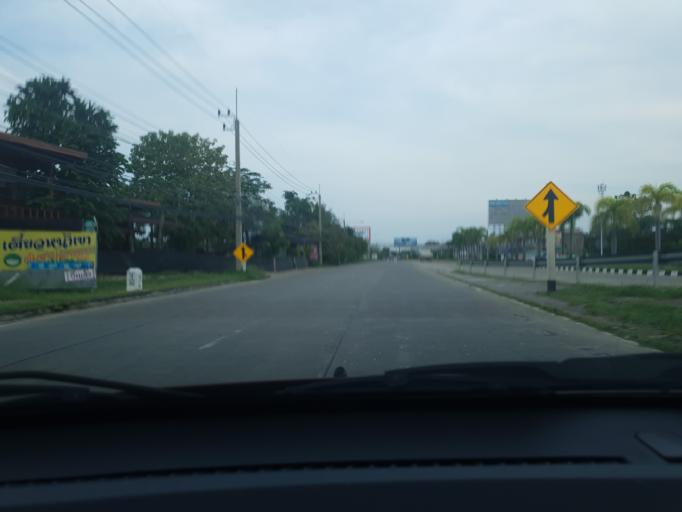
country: TH
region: Phetchaburi
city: Cha-am
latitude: 12.8087
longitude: 99.9459
